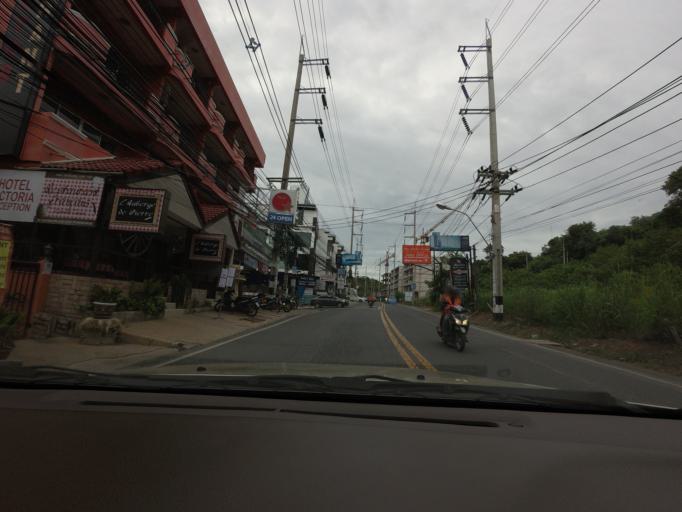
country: TH
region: Chon Buri
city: Phatthaya
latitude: 12.9154
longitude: 100.8668
